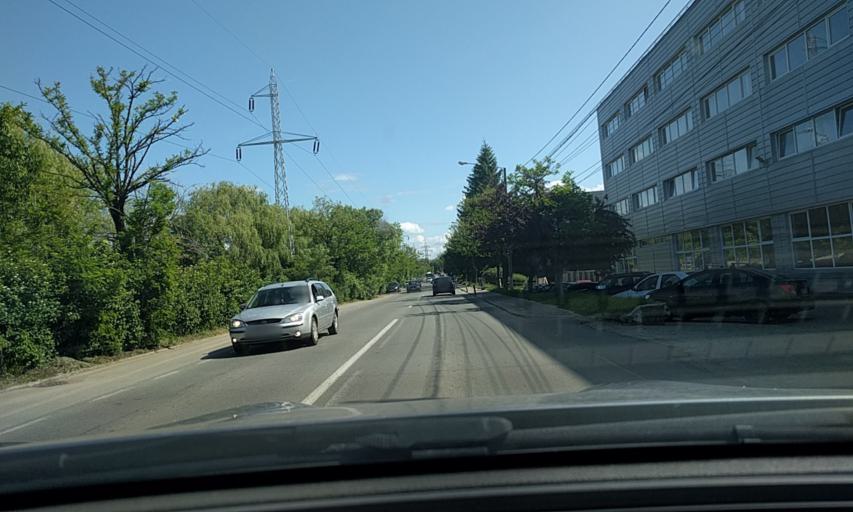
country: RO
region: Bistrita-Nasaud
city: Bistrita
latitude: 47.1303
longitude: 24.4698
